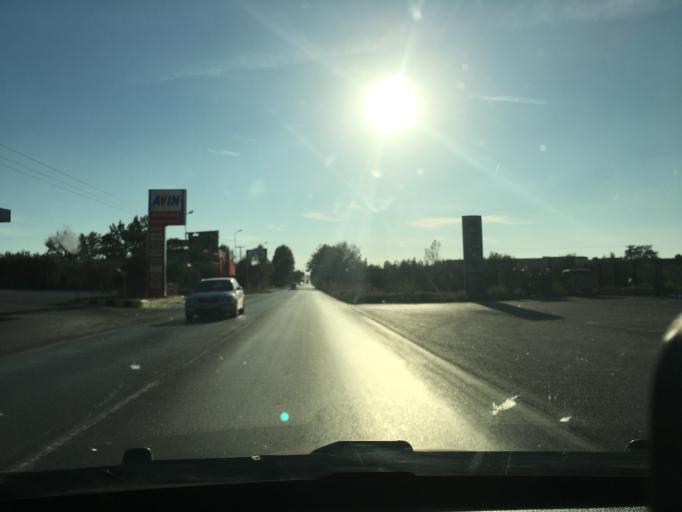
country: GR
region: Central Macedonia
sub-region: Nomos Chalkidikis
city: Nea Moudhania
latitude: 40.2516
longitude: 23.3161
